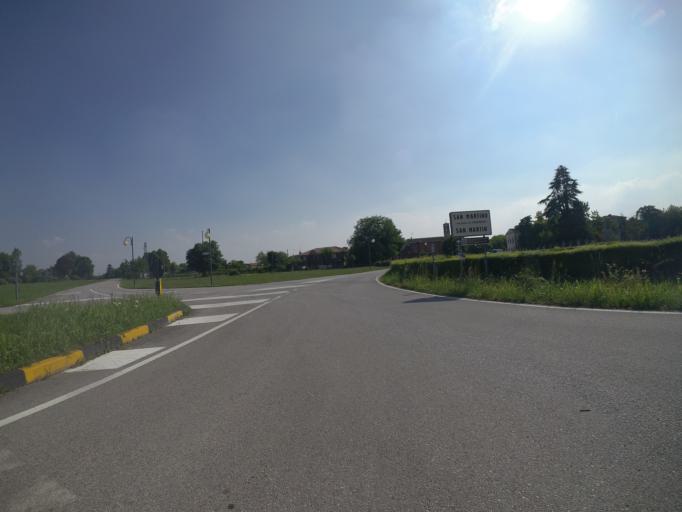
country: IT
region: Friuli Venezia Giulia
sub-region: Provincia di Udine
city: Varmo
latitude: 45.9197
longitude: 12.9936
